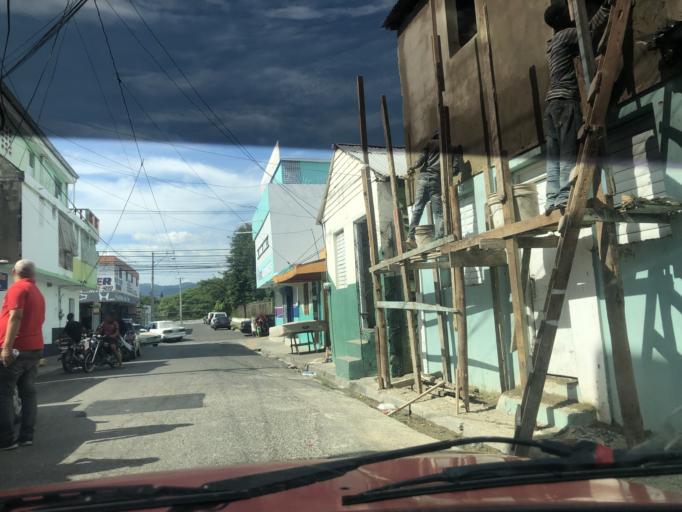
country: DO
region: Santiago
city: Santiago de los Caballeros
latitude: 19.4621
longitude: -70.7077
